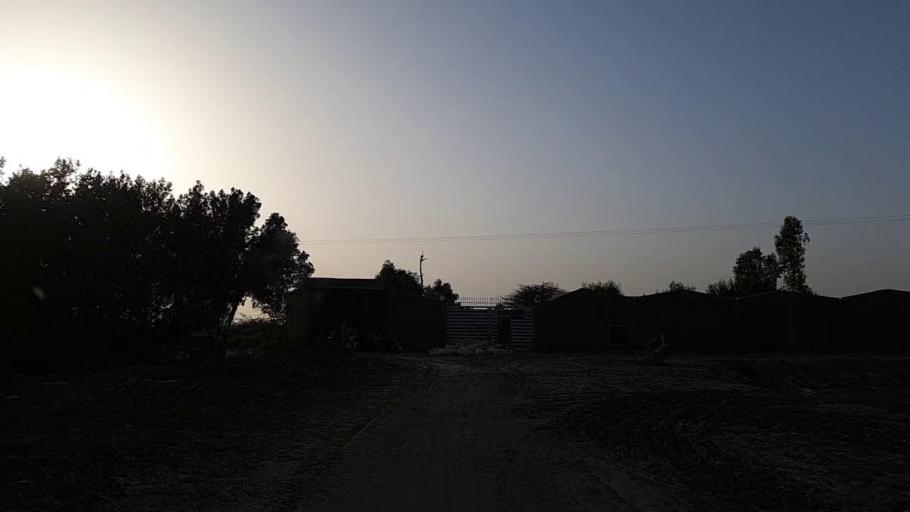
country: PK
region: Sindh
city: Jati
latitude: 24.4192
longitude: 68.1907
